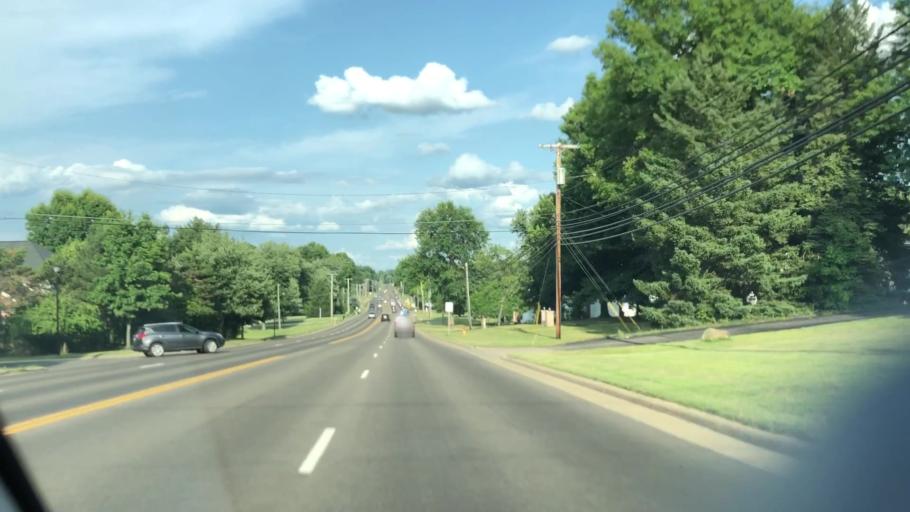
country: US
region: Ohio
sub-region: Summit County
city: Greensburg
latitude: 40.8785
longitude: -81.4662
